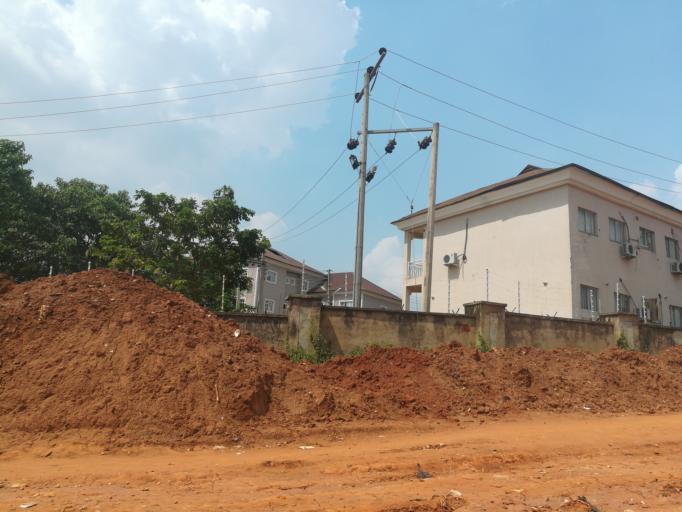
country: NG
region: Abuja Federal Capital Territory
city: Abuja
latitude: 9.0585
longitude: 7.4519
